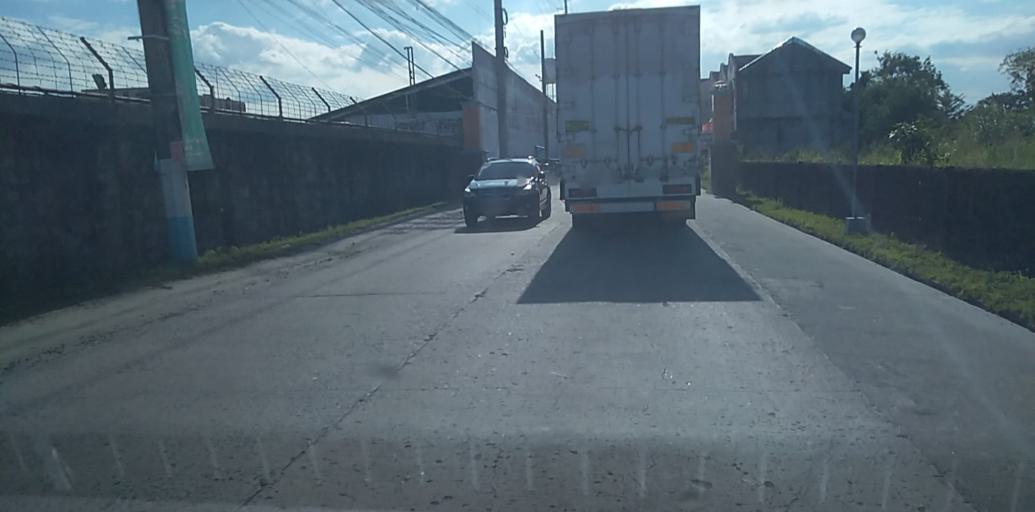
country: PH
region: Central Luzon
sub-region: Province of Pampanga
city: Telabastagan
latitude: 15.1029
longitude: 120.6212
